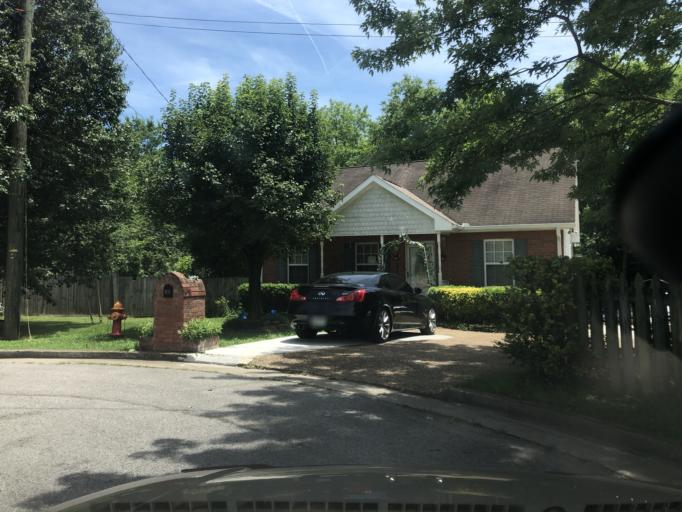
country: US
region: Tennessee
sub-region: Davidson County
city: Goodlettsville
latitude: 36.2593
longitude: -86.7055
